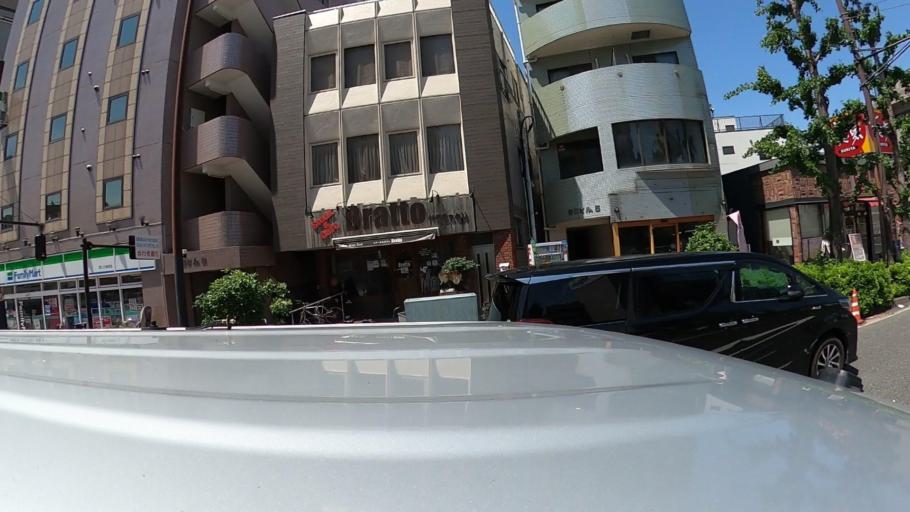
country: JP
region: Kanagawa
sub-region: Kawasaki-shi
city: Kawasaki
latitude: 35.5541
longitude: 139.7399
